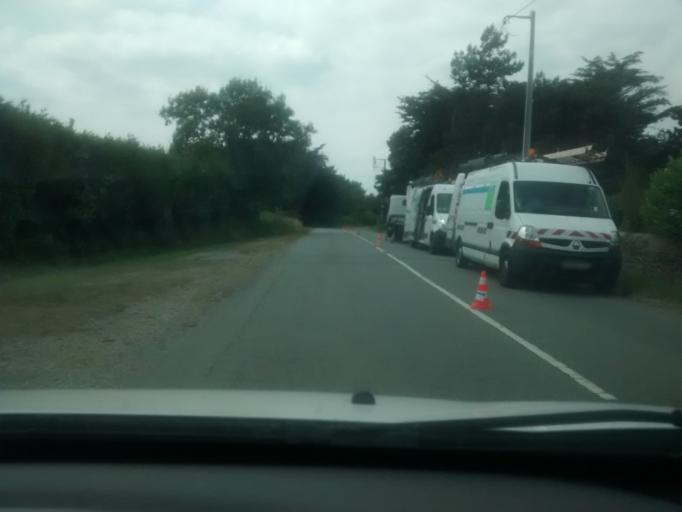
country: FR
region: Brittany
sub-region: Departement d'Ille-et-Vilaine
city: Saint-Lunaire
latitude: 48.6300
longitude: -2.0927
